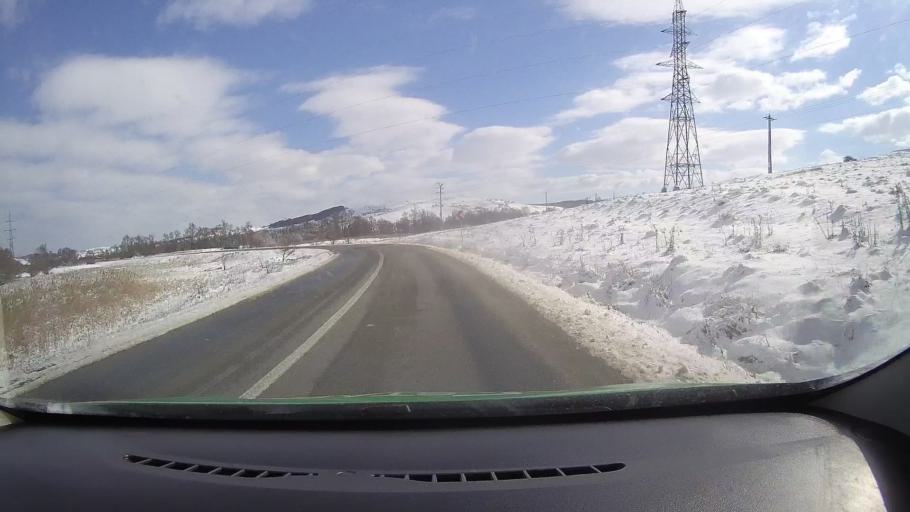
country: RO
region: Sibiu
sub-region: Comuna Barghis
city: Barghis
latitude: 45.9616
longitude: 24.5633
